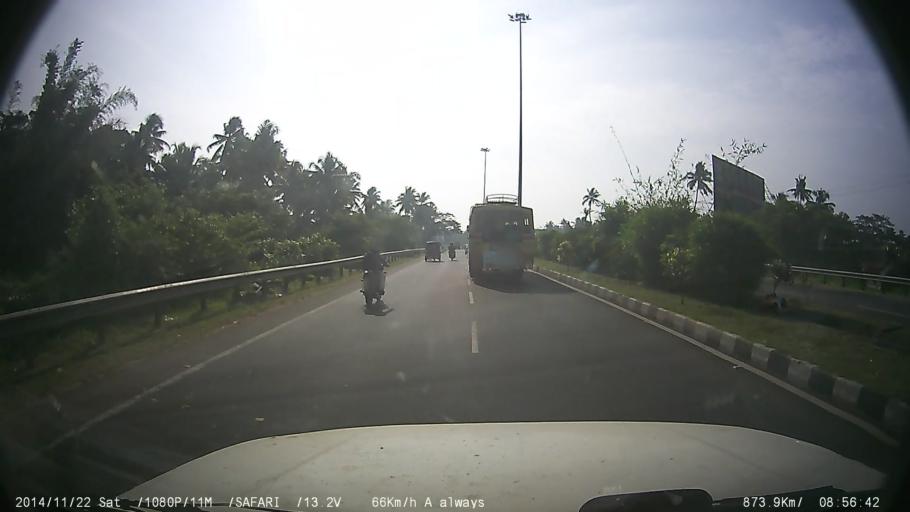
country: IN
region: Kerala
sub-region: Thrissur District
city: Irinjalakuda
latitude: 10.4131
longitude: 76.2710
